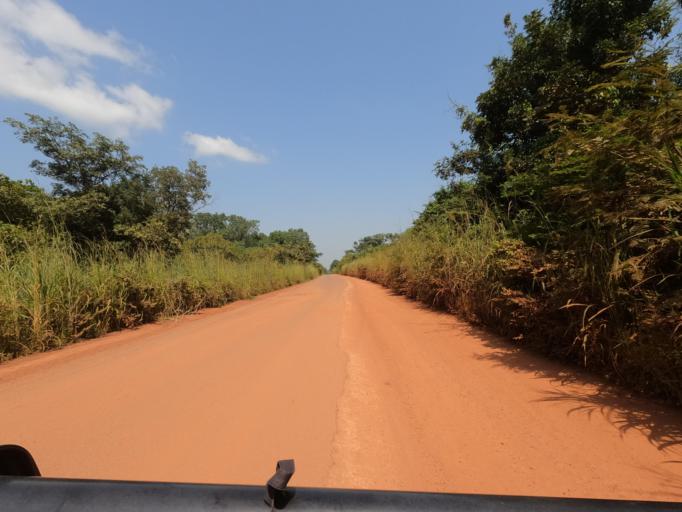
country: GW
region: Oio
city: Bissora
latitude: 12.3502
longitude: -15.7644
